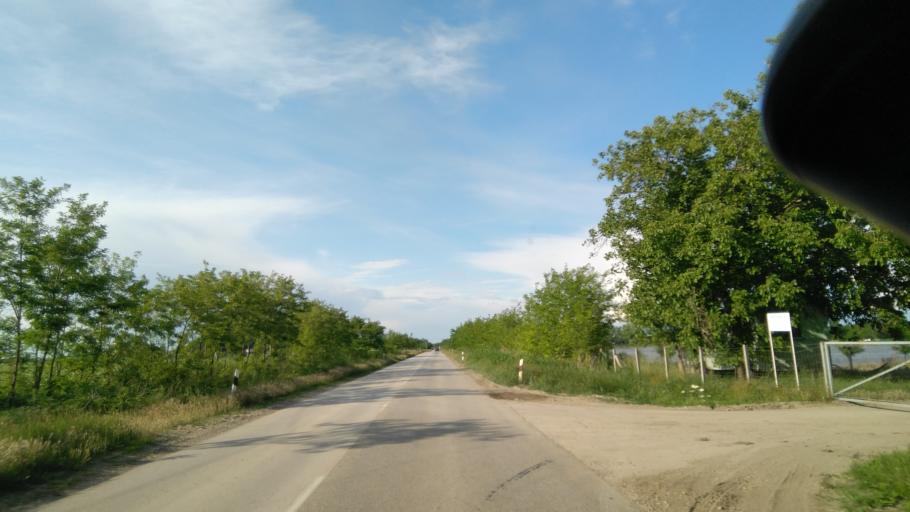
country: HU
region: Bekes
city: Elek
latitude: 46.5735
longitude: 21.2702
